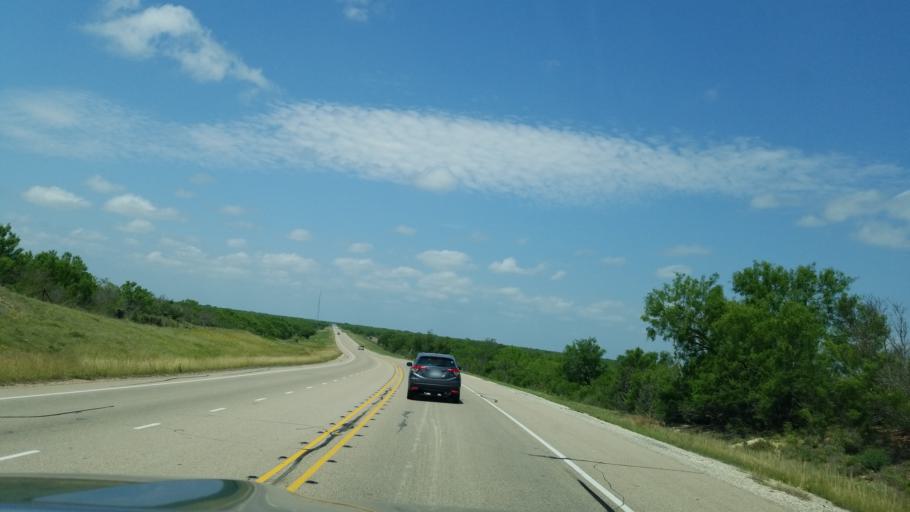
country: US
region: Texas
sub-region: Frio County
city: Pearsall
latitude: 29.0141
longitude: -99.1179
